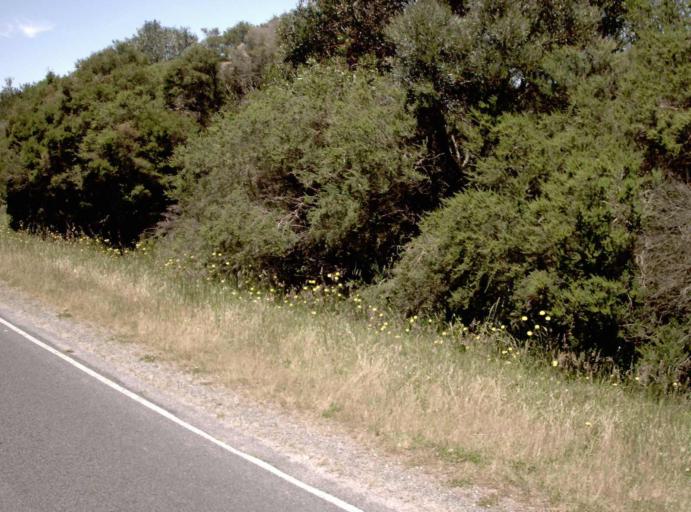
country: AU
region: Victoria
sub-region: Latrobe
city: Morwell
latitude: -38.7999
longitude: 146.1894
